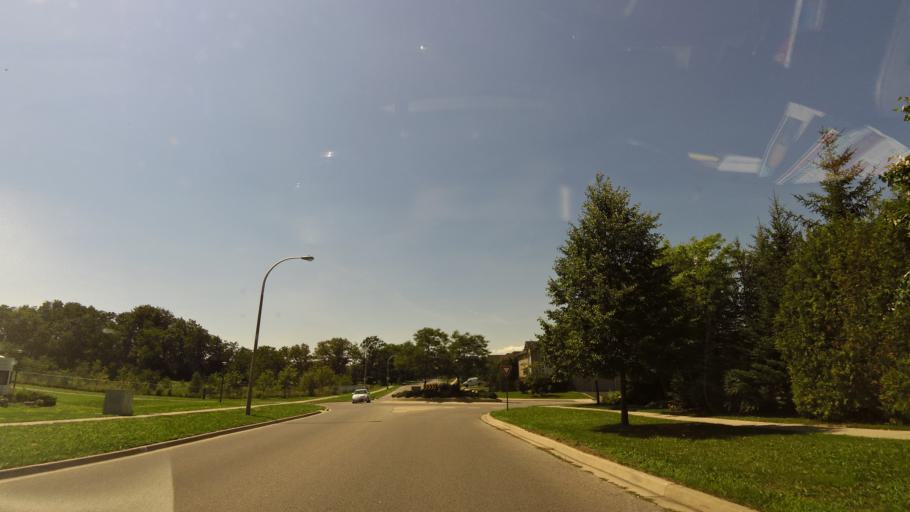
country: CA
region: Ontario
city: Ancaster
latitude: 43.2166
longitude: -79.9509
